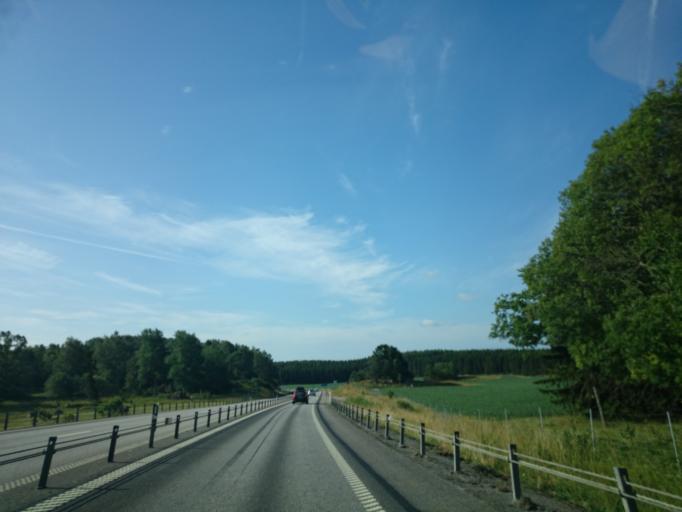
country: SE
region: OEstergoetland
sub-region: Soderkopings Kommun
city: Soederkoeping
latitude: 58.3927
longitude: 16.4107
